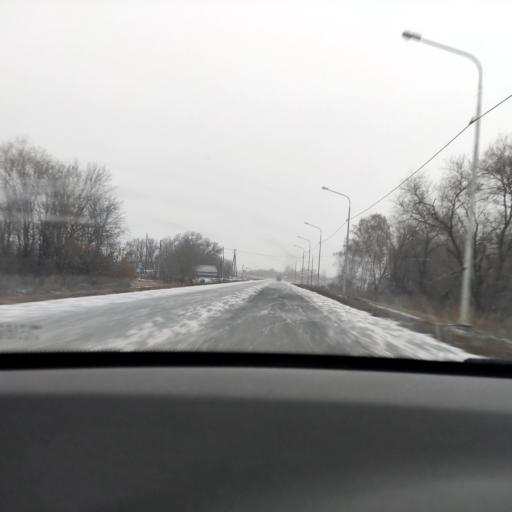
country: RU
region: Samara
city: Krasnoarmeyskoye
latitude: 52.8960
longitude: 49.9665
